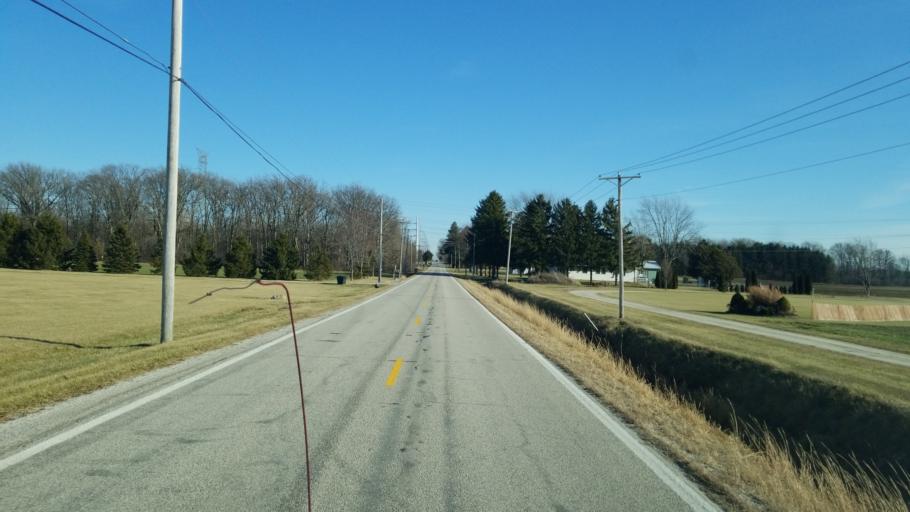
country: US
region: Ohio
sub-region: Wood County
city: Luckey
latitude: 41.4500
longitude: -83.4479
